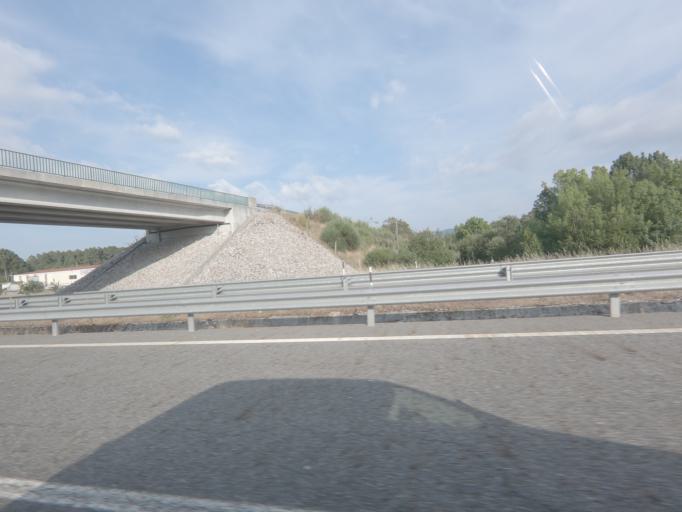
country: PT
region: Vila Real
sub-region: Chaves
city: Chaves
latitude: 41.7494
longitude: -7.5214
